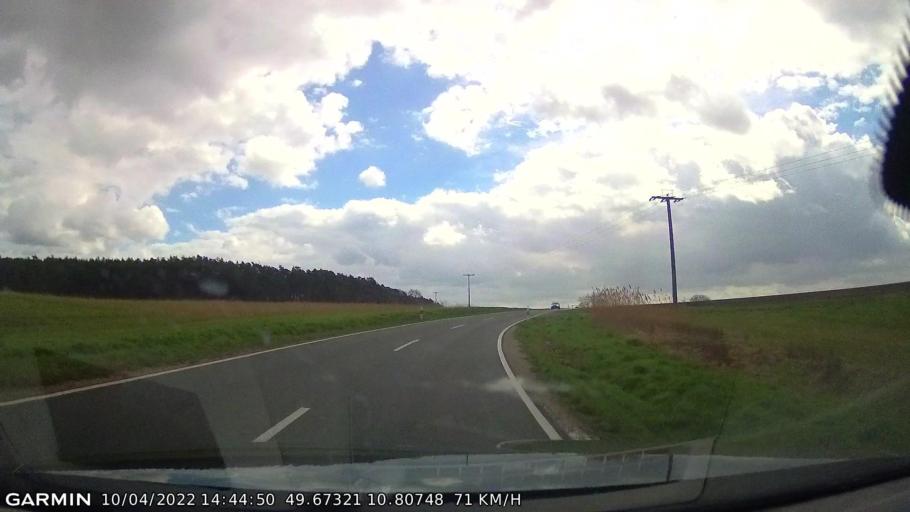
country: DE
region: Bavaria
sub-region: Regierungsbezirk Mittelfranken
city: Gremsdorf
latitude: 49.6730
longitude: 10.8073
